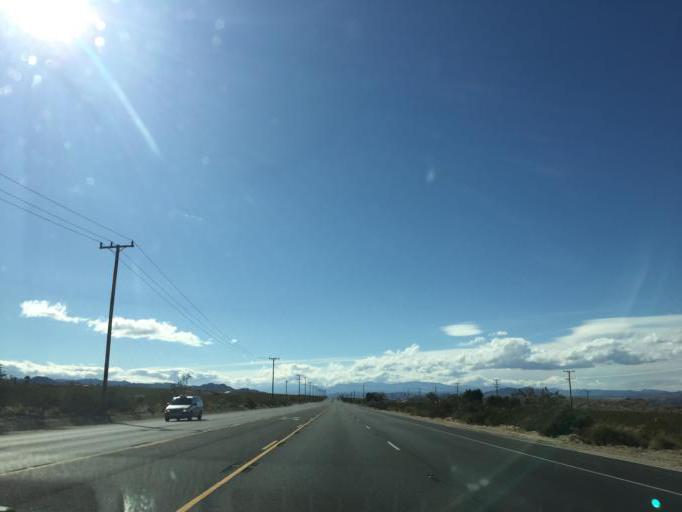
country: US
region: California
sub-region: San Bernardino County
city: Twentynine Palms
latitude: 34.1352
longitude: -116.1820
